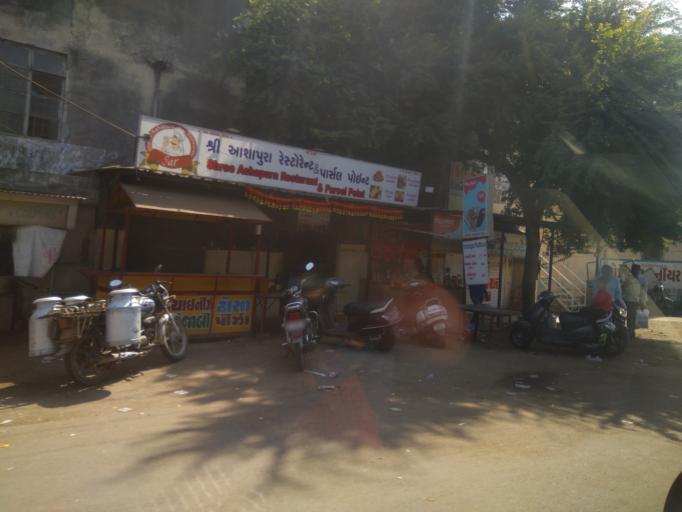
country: IN
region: Gujarat
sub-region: Jamnagar
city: Jamnagar
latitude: 22.4440
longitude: 70.0656
